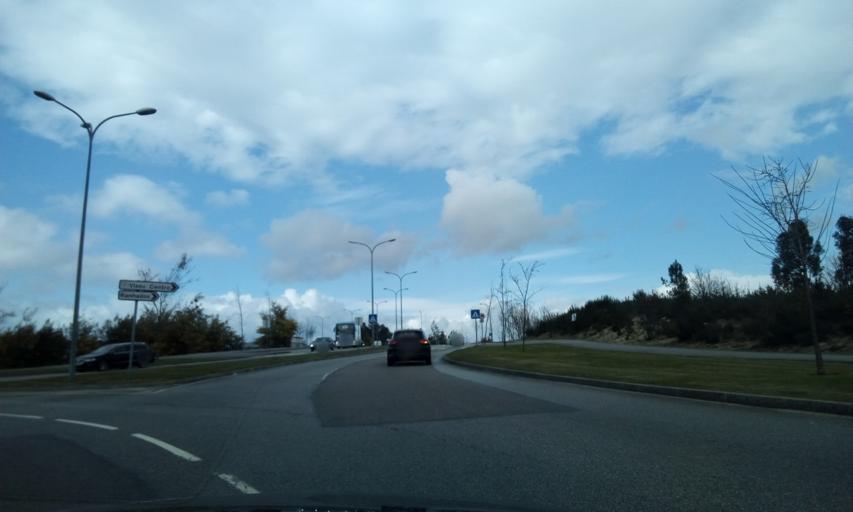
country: PT
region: Viseu
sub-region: Viseu
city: Viseu
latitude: 40.6337
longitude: -7.9073
